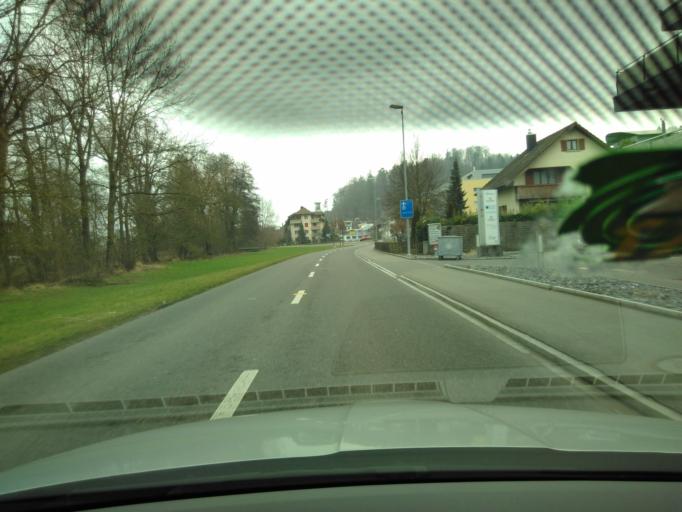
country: CH
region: Aargau
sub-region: Bezirk Aarau
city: Muhen
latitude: 47.3307
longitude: 8.0557
